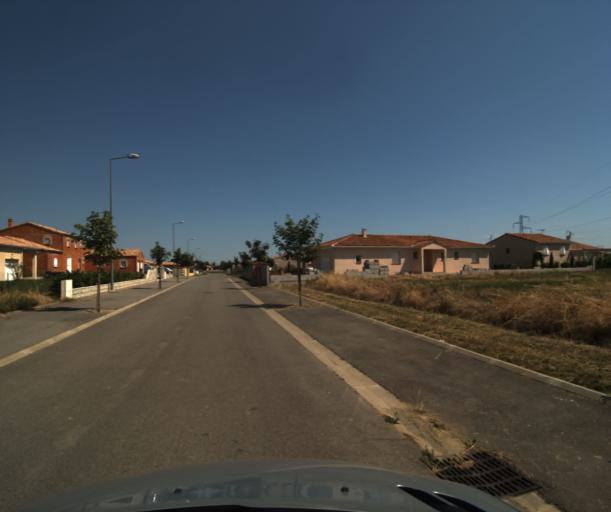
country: FR
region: Midi-Pyrenees
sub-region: Departement de la Haute-Garonne
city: Saubens
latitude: 43.4808
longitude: 1.3551
